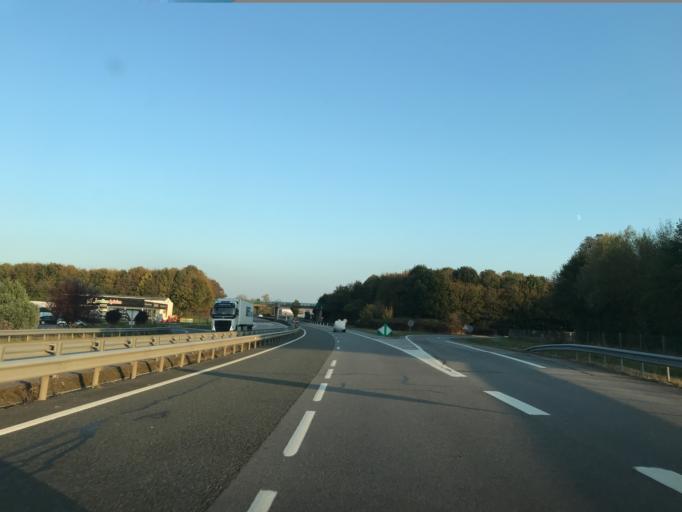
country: FR
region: Pays de la Loire
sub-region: Departement de la Sarthe
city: Mamers
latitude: 48.5060
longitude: 0.3574
